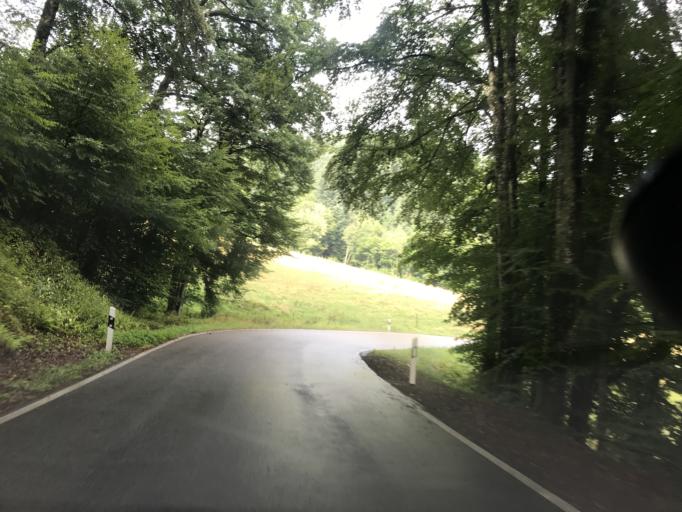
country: DE
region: Baden-Wuerttemberg
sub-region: Freiburg Region
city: Kandern
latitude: 47.7010
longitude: 7.7096
